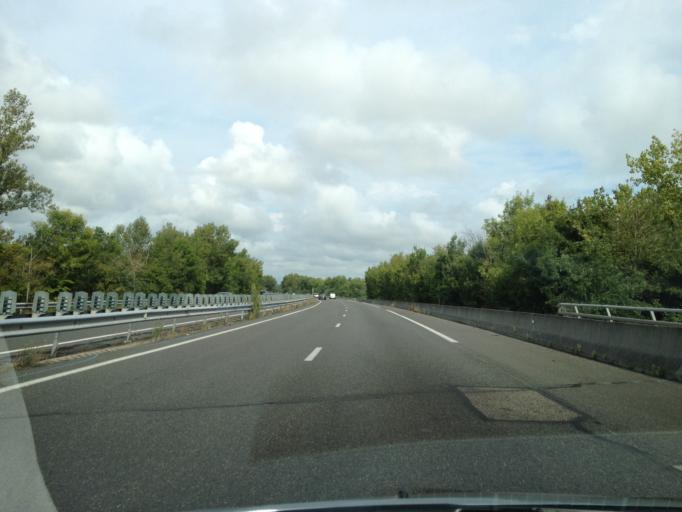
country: FR
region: Aquitaine
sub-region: Departement du Lot-et-Garonne
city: Layrac
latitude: 44.1404
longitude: 0.6674
